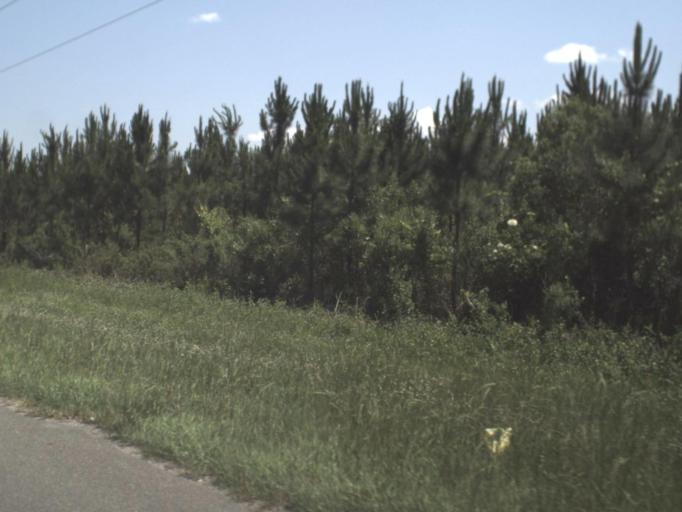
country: US
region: Florida
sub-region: Bradford County
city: Starke
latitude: 29.8782
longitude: -82.0801
